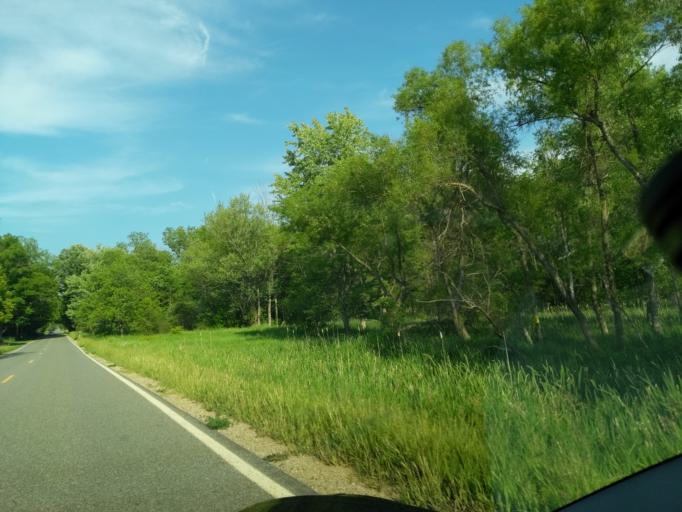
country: US
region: Michigan
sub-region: Barry County
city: Nashville
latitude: 42.6250
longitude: -85.1313
